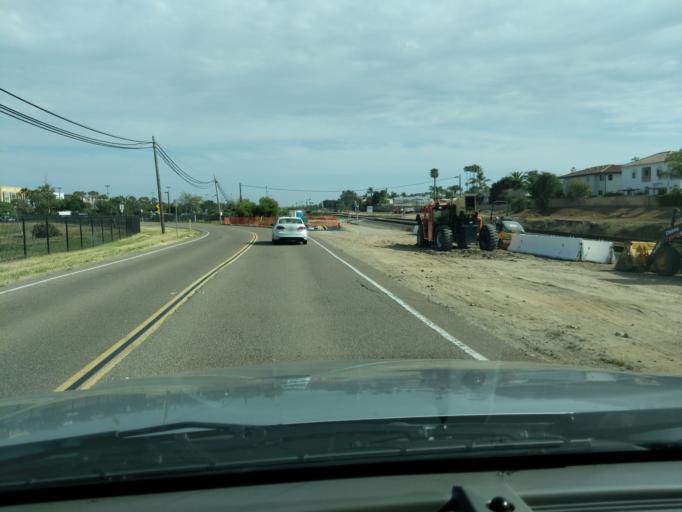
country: US
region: California
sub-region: San Diego County
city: Carlsbad
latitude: 33.1115
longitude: -117.3201
